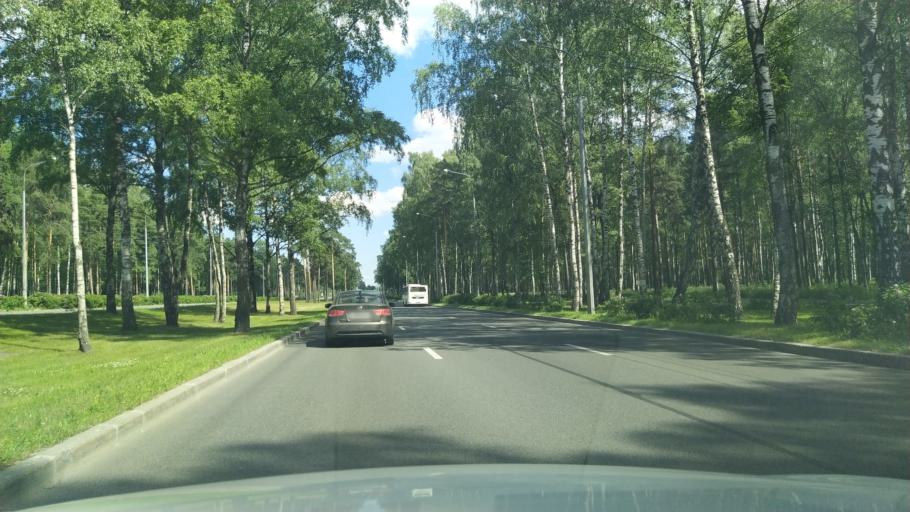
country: RU
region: Leningrad
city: Kalininskiy
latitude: 59.9946
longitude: 30.3943
